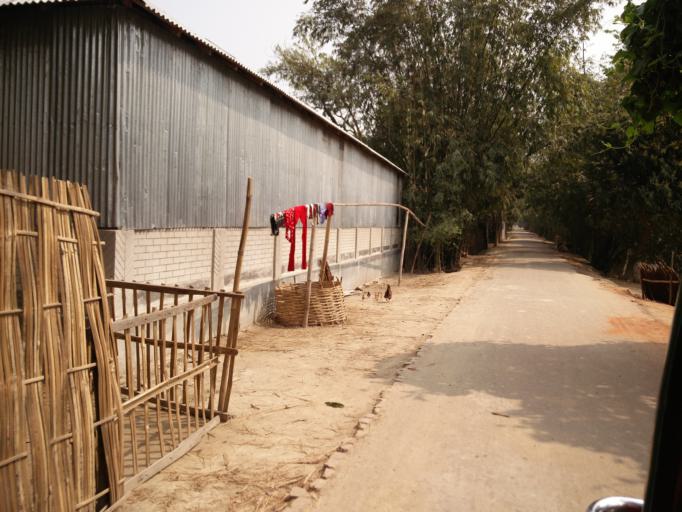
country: BD
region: Rangpur Division
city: Nageswari
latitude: 25.8896
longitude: 89.7215
